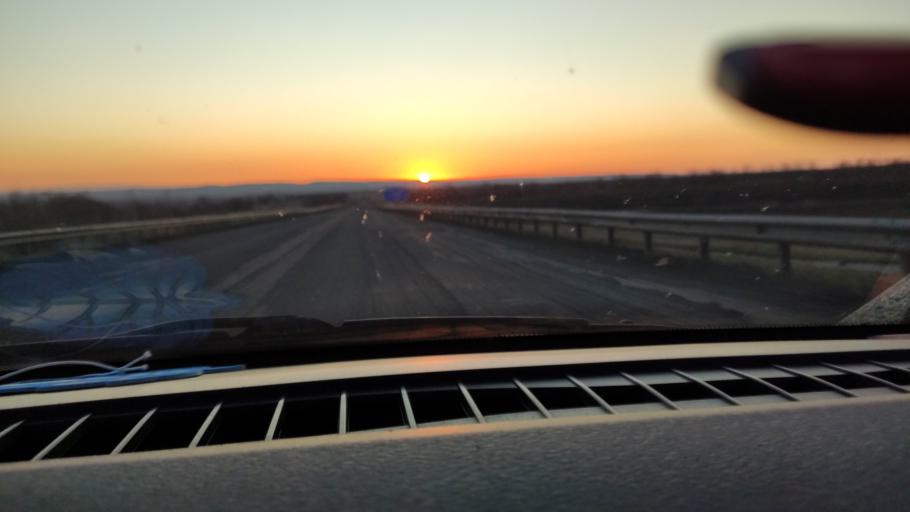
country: RU
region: Saratov
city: Yelshanka
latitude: 51.7931
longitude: 46.1602
